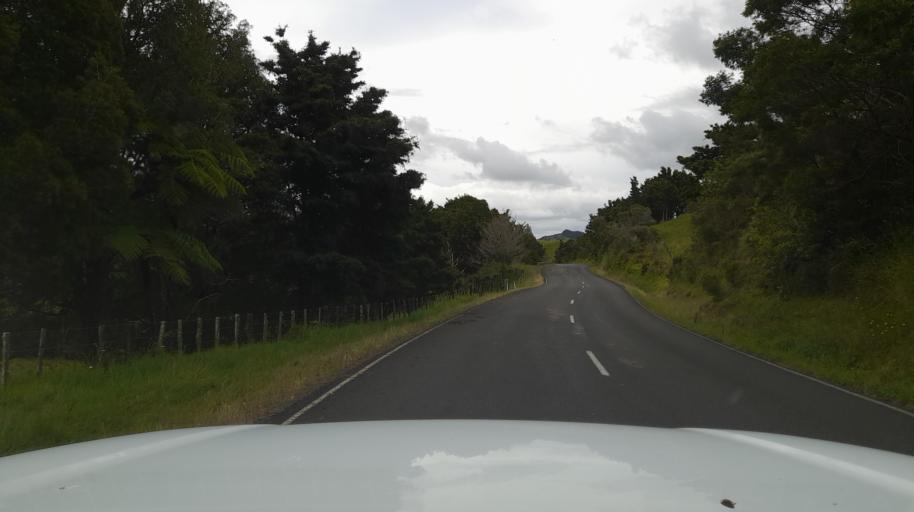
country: NZ
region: Northland
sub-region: Far North District
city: Kaitaia
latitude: -35.2806
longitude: 173.3720
